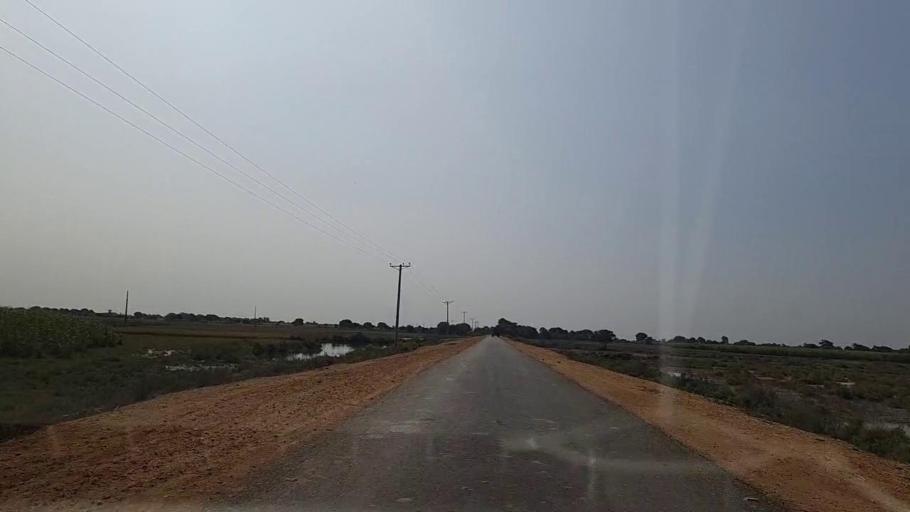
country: PK
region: Sindh
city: Chuhar Jamali
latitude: 24.3507
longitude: 67.9534
